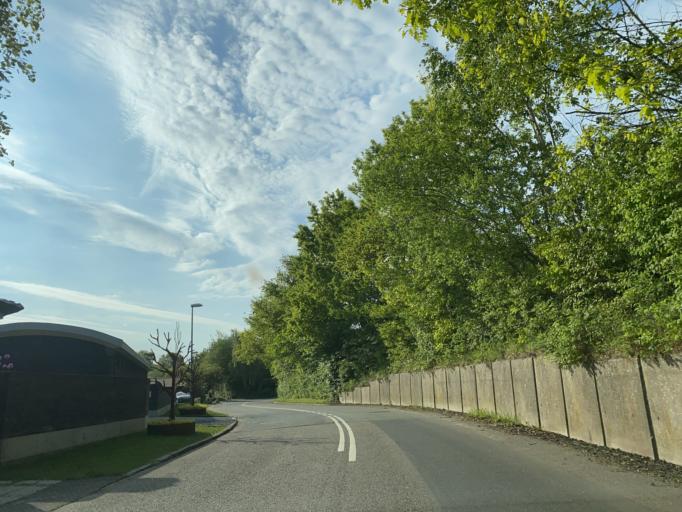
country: DK
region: South Denmark
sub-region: Sonderborg Kommune
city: Dybbol
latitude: 54.9154
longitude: 9.7669
